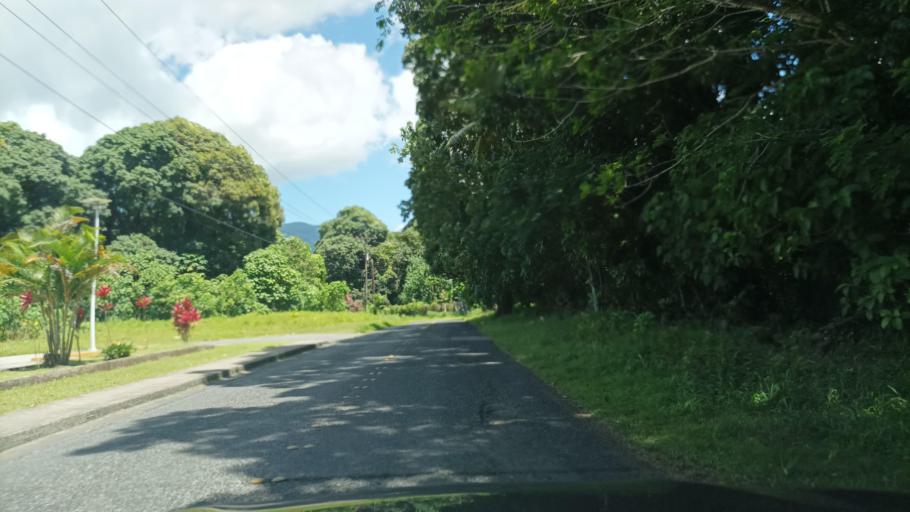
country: FM
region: Pohnpei
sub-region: Kolonia Municipality
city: Kolonia
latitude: 6.9561
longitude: 158.2165
